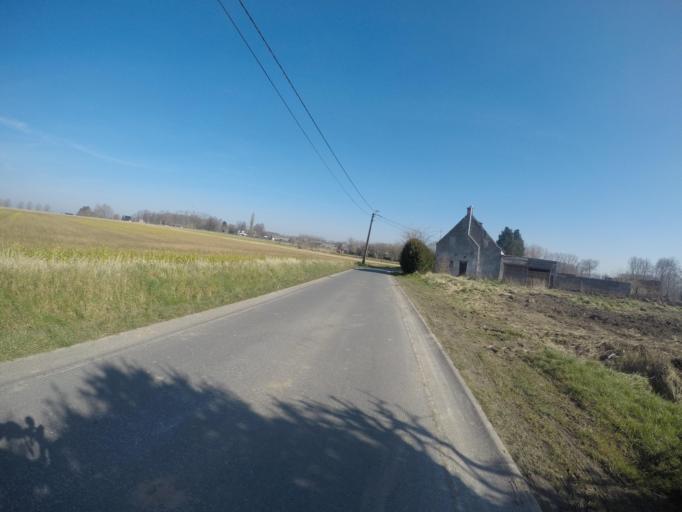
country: BE
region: Flanders
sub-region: Provincie Oost-Vlaanderen
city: Sint-Maria-Lierde
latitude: 50.8059
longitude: 3.7916
